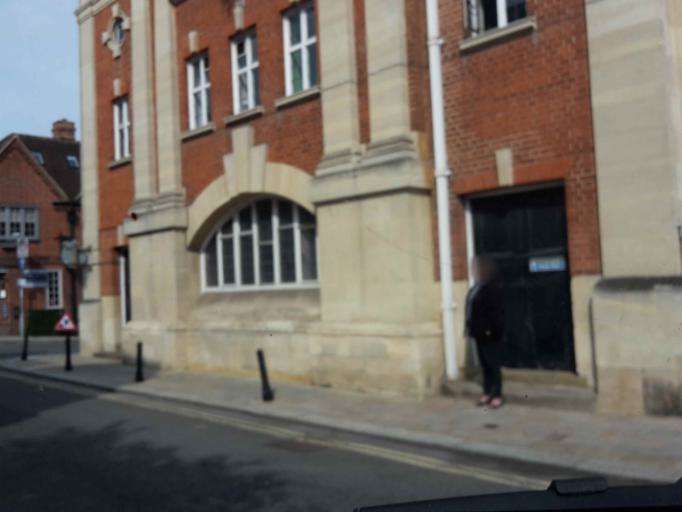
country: GB
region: England
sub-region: Oxfordshire
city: Henley on Thames
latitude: 51.5372
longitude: -0.9066
